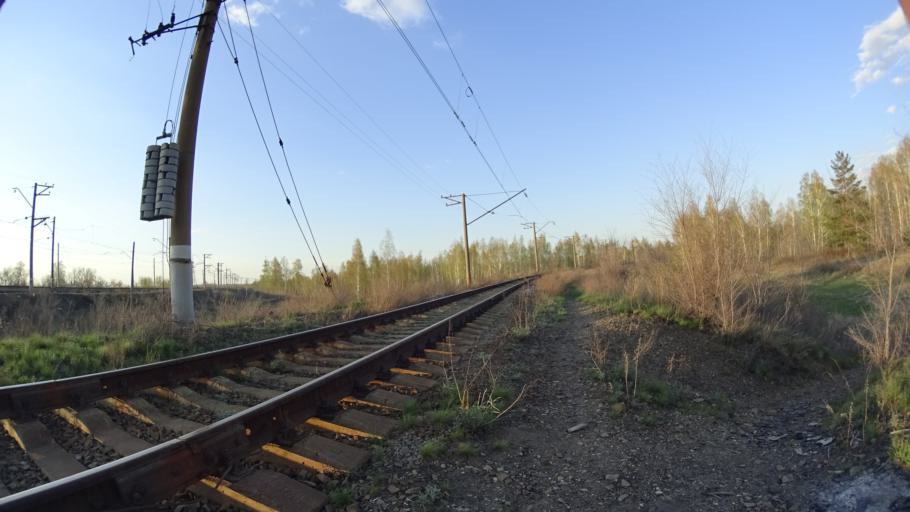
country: RU
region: Chelyabinsk
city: Troitsk
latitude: 54.0579
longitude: 61.6143
